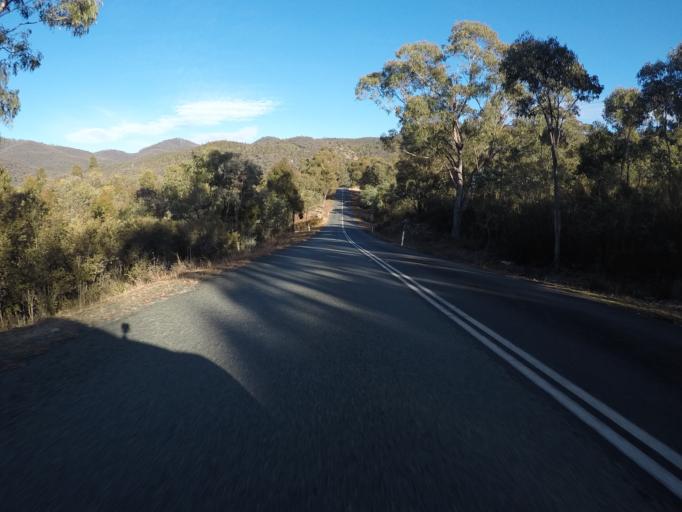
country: AU
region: Australian Capital Territory
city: Macarthur
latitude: -35.4682
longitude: 148.9600
